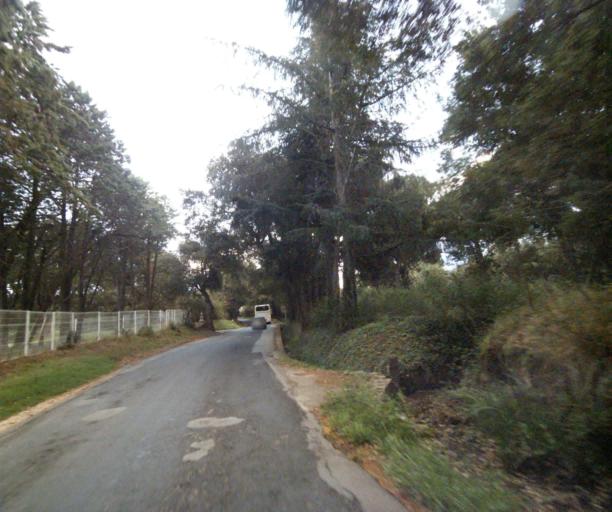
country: FR
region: Languedoc-Roussillon
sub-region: Departement des Pyrenees-Orientales
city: Argelers
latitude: 42.5618
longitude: 3.0166
